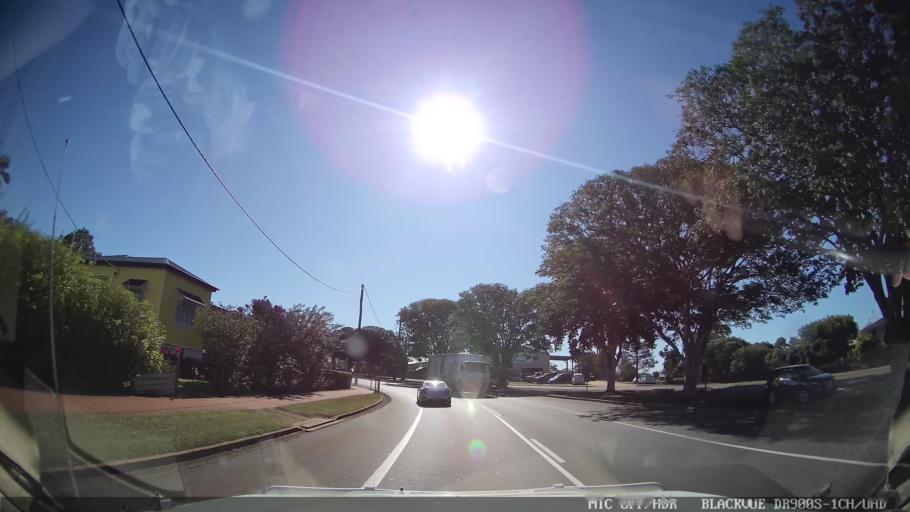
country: AU
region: Queensland
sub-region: Bundaberg
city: Childers
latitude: -25.2338
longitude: 152.2734
